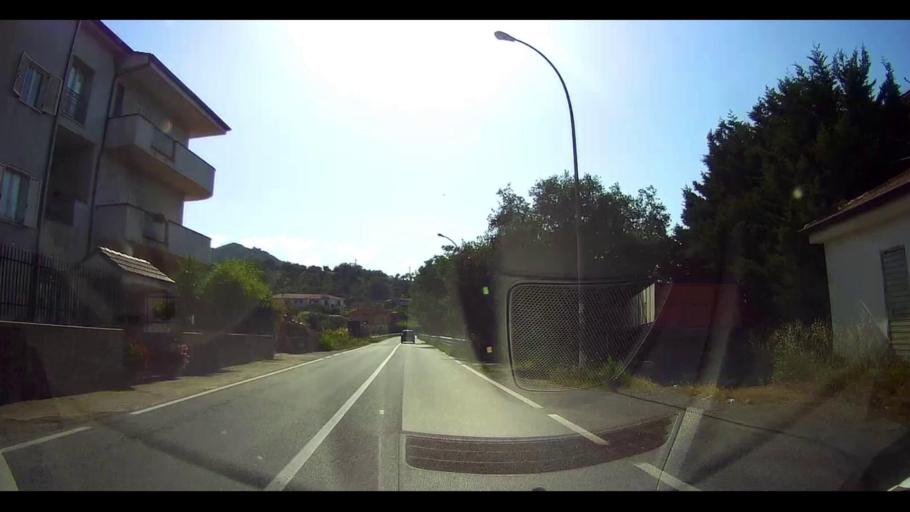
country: IT
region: Calabria
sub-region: Provincia di Cosenza
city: Cariati
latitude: 39.4843
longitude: 16.9718
